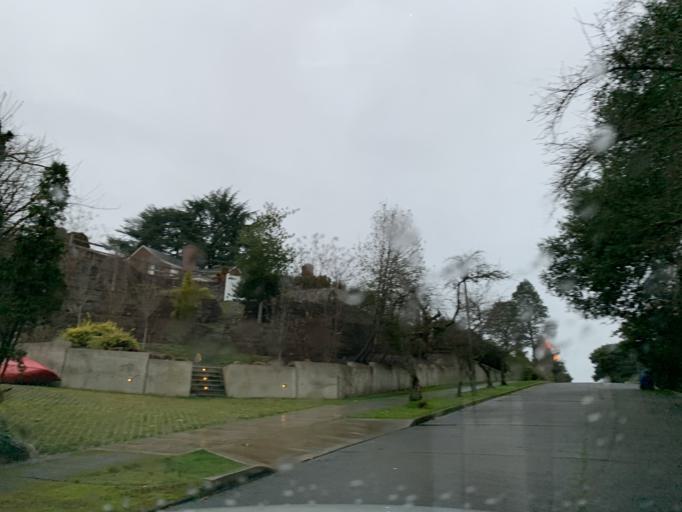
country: US
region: Washington
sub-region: King County
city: Yarrow Point
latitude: 47.6684
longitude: -122.2618
